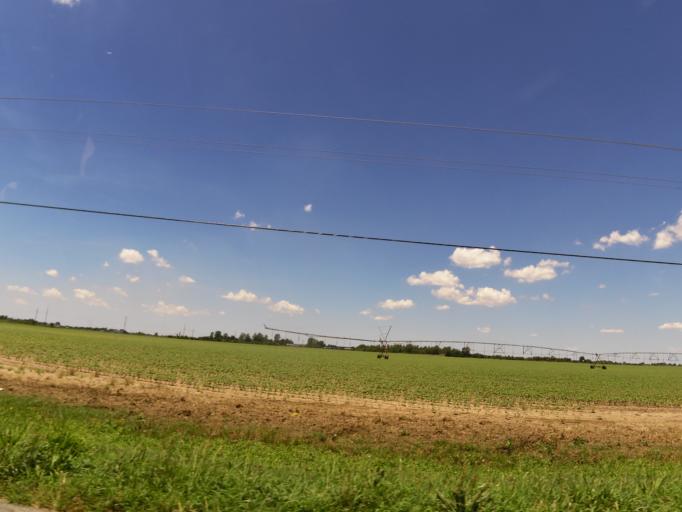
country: US
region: Missouri
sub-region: New Madrid County
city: New Madrid
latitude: 36.5775
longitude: -89.5631
